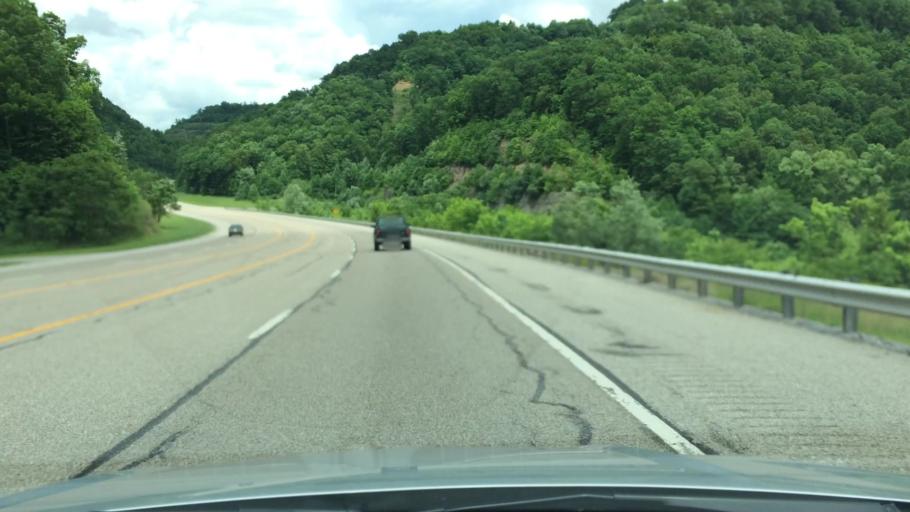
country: US
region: Kentucky
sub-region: Letcher County
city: Jenkins
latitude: 37.1997
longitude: -82.6220
